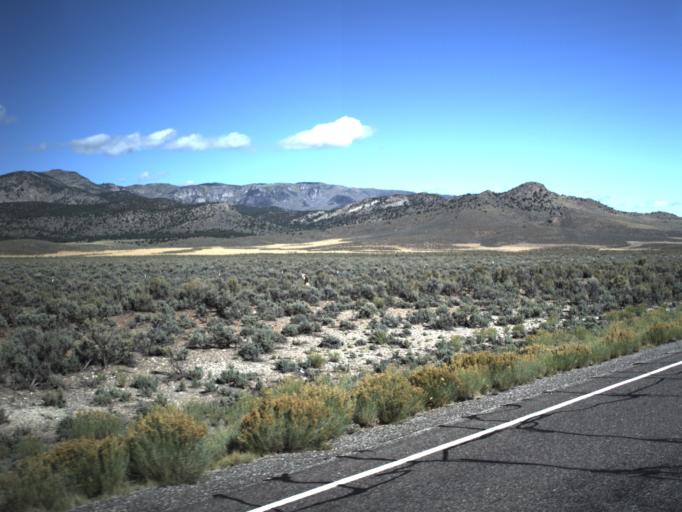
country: US
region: Utah
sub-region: Piute County
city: Junction
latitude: 38.2842
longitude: -111.9801
